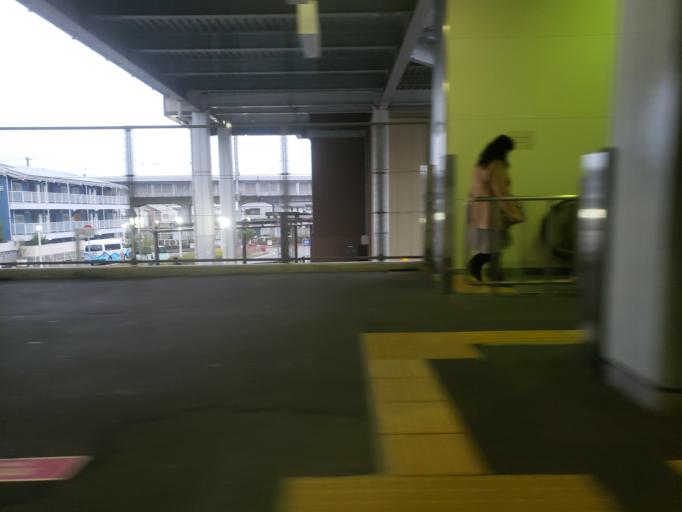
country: JP
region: Hyogo
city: Akashi
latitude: 34.6962
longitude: 134.9061
